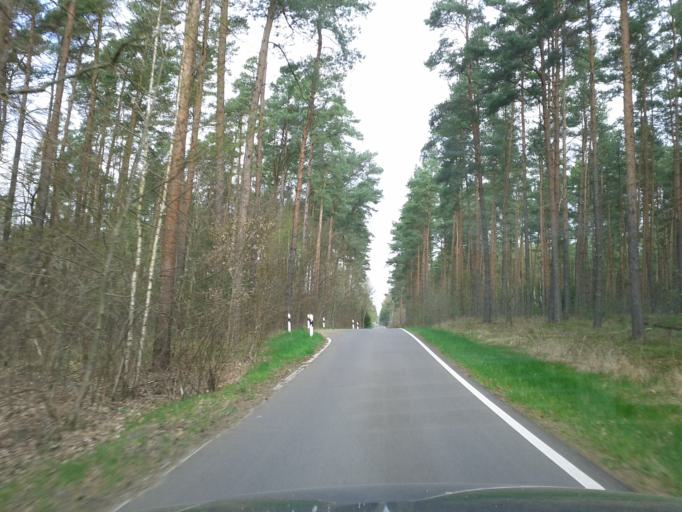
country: DE
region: Brandenburg
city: Spreenhagen
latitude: 52.3849
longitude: 13.8527
